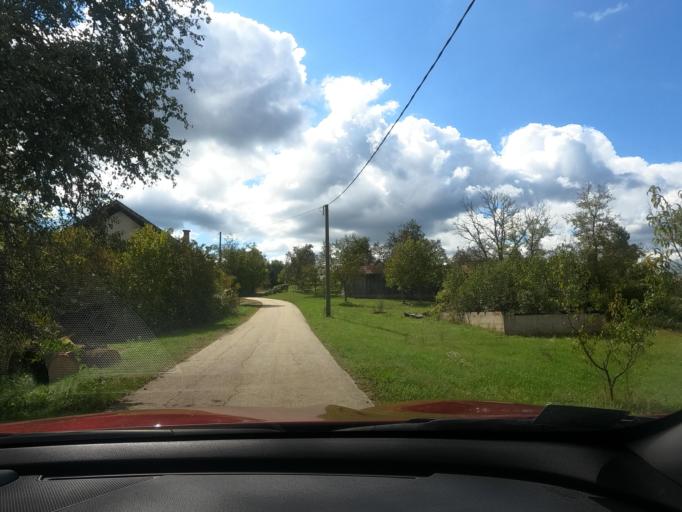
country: HR
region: Karlovacka
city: Vojnic
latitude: 45.2370
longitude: 15.7072
